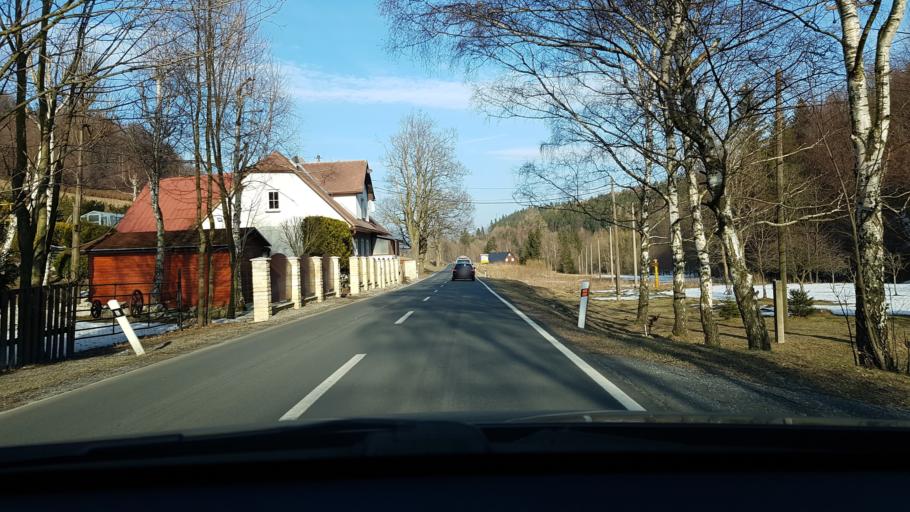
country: CZ
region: Olomoucky
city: Vapenna
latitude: 50.2121
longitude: 17.0980
